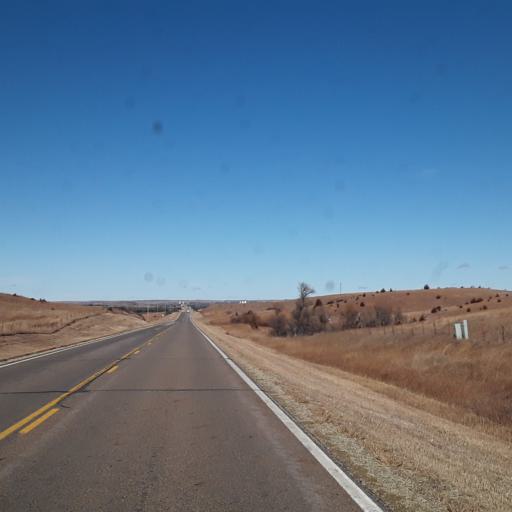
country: US
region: Kansas
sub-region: Lincoln County
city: Lincoln
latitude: 38.9537
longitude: -98.1511
